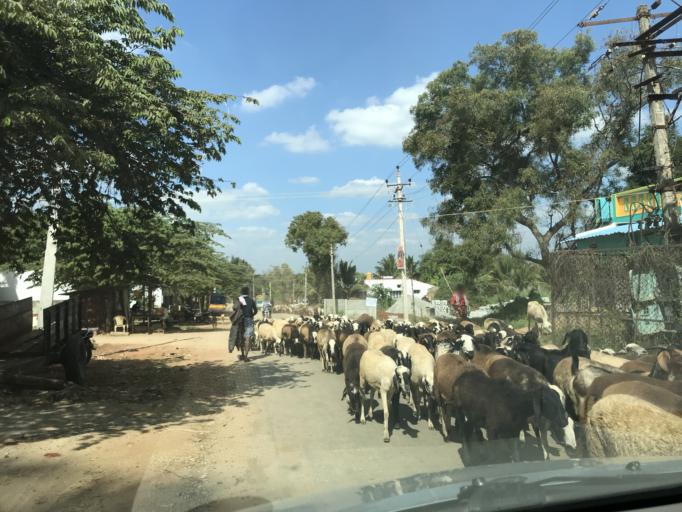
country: IN
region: Karnataka
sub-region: Mandya
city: Krishnarajpet
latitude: 12.6655
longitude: 76.3842
